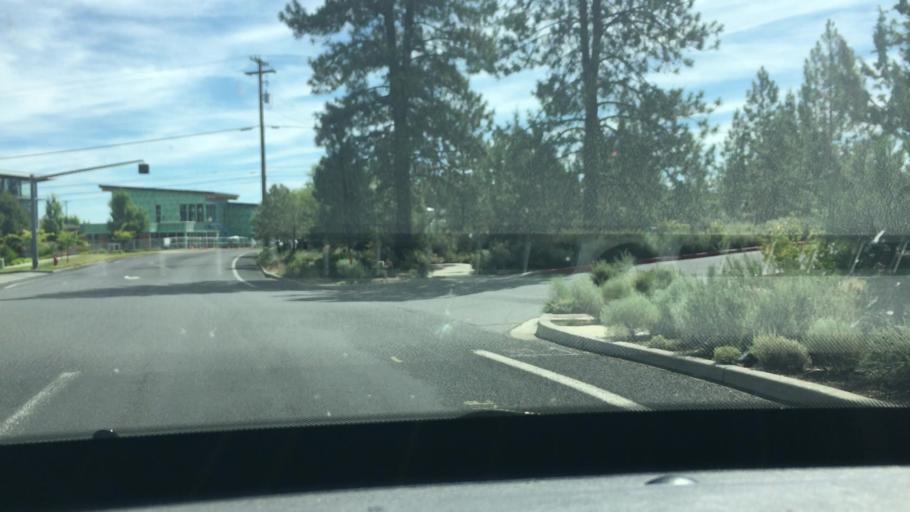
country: US
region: Oregon
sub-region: Deschutes County
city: Bend
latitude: 44.0479
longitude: -121.3296
